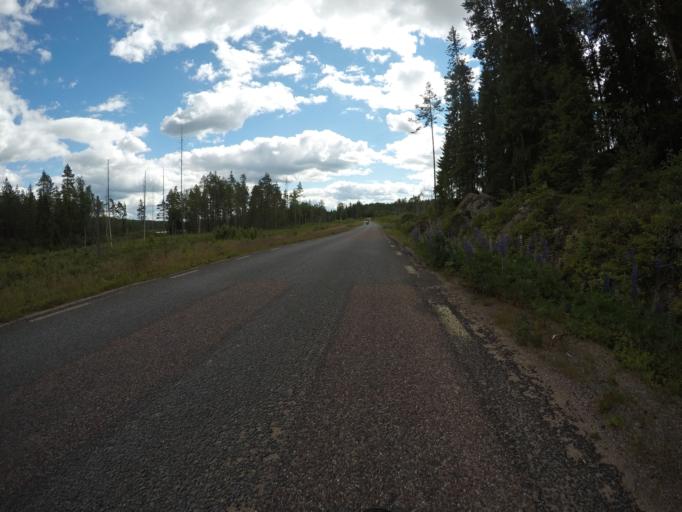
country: SE
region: OErebro
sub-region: Hallefors Kommun
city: Haellefors
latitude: 60.0797
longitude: 14.4846
